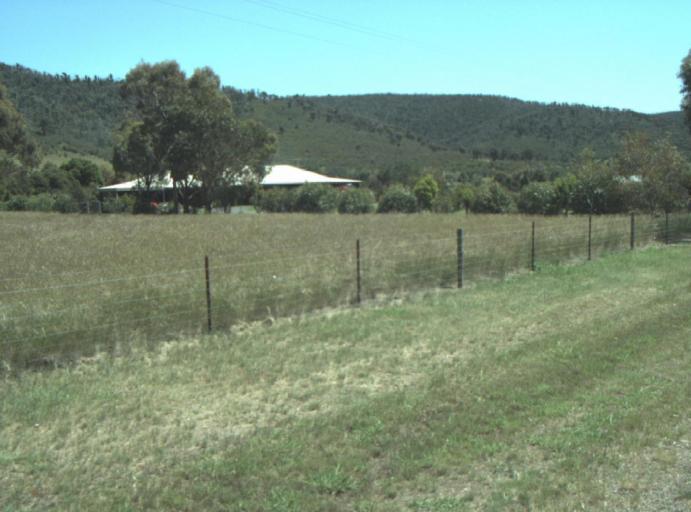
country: AU
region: Victoria
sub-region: Greater Geelong
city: Lara
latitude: -37.8585
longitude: 144.2801
